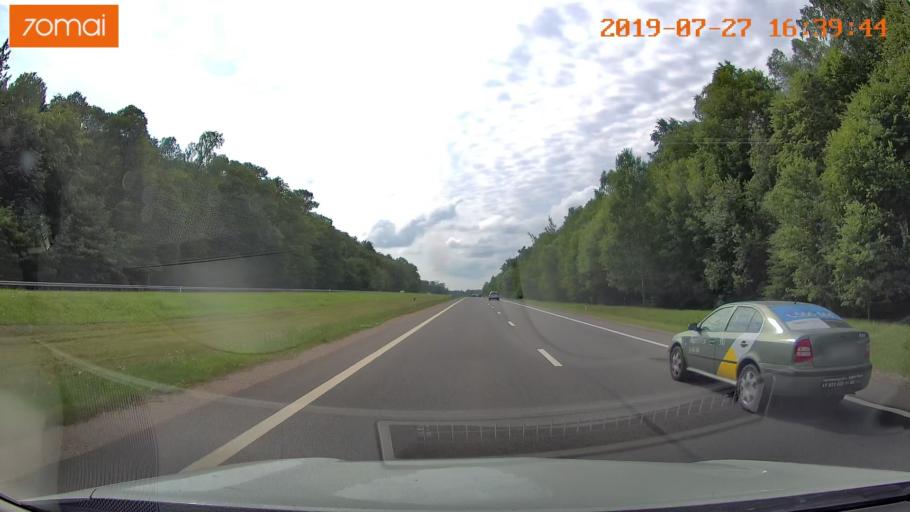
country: RU
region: Kaliningrad
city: Gvardeysk
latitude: 54.6496
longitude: 21.1926
